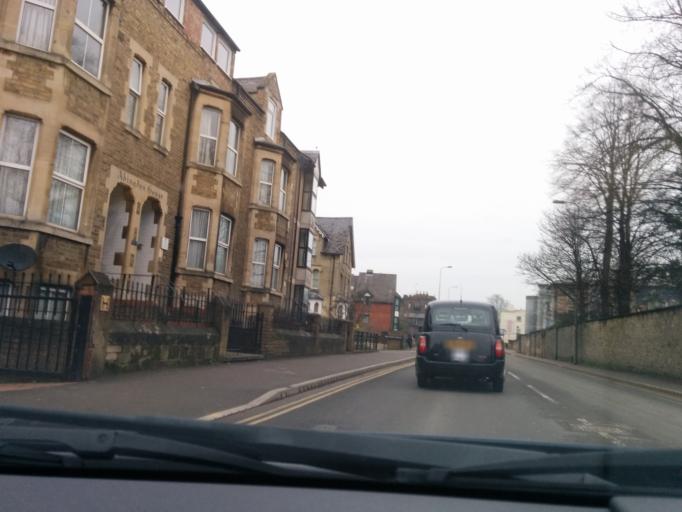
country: GB
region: England
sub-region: Oxfordshire
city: Oxford
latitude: 51.7447
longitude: -1.2561
